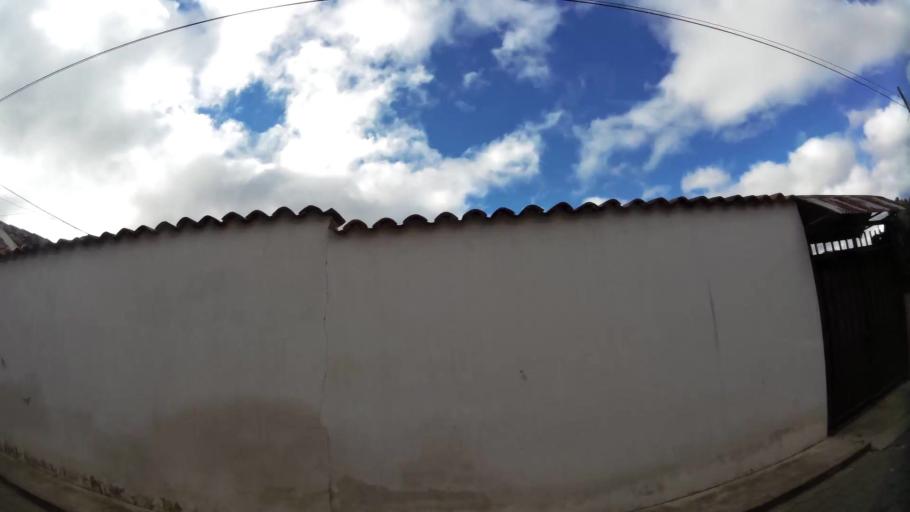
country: GT
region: Quetzaltenango
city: Salcaja
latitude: 14.8797
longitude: -91.4543
